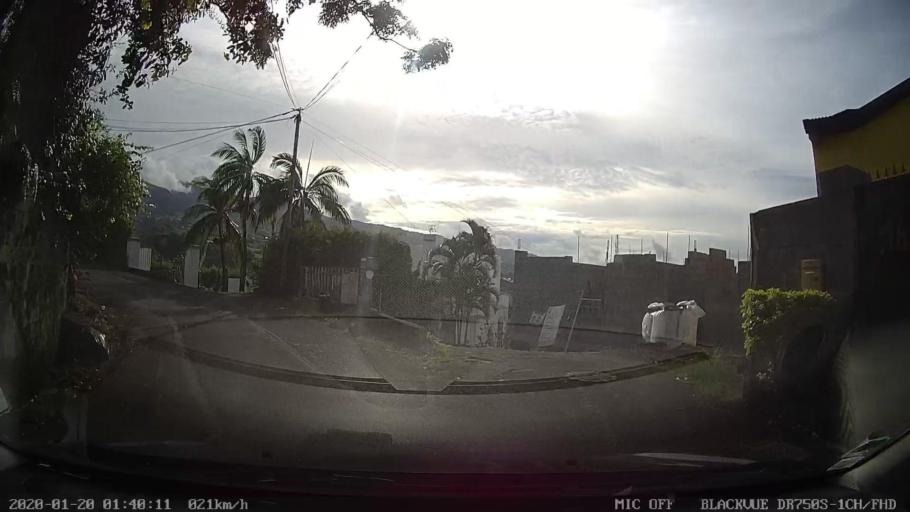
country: RE
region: Reunion
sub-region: Reunion
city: Sainte-Marie
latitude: -20.9211
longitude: 55.5152
